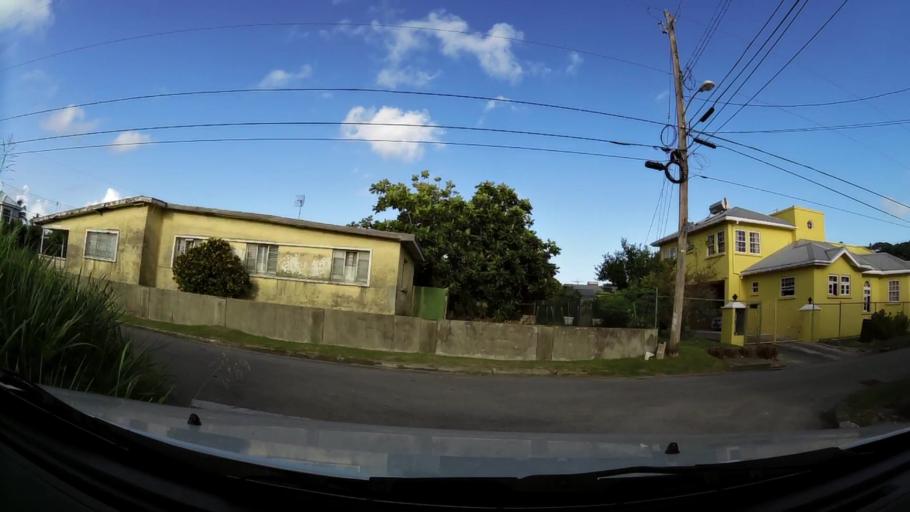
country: BB
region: Christ Church
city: Oistins
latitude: 13.0685
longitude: -59.5534
